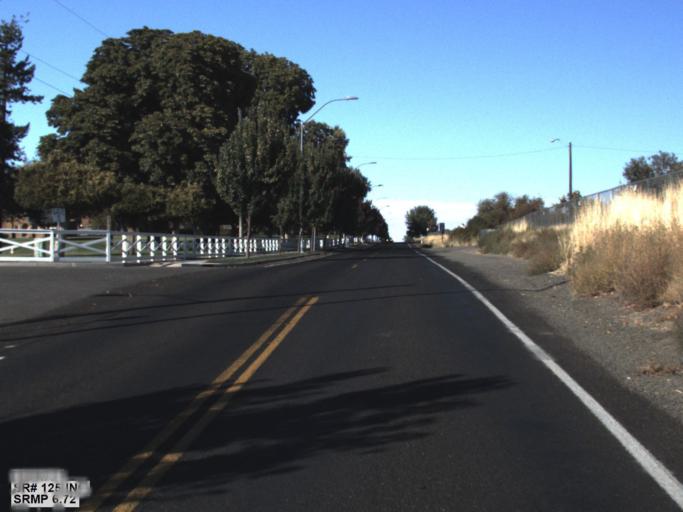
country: US
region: Washington
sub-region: Walla Walla County
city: Walla Walla
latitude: 46.0779
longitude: -118.3564
